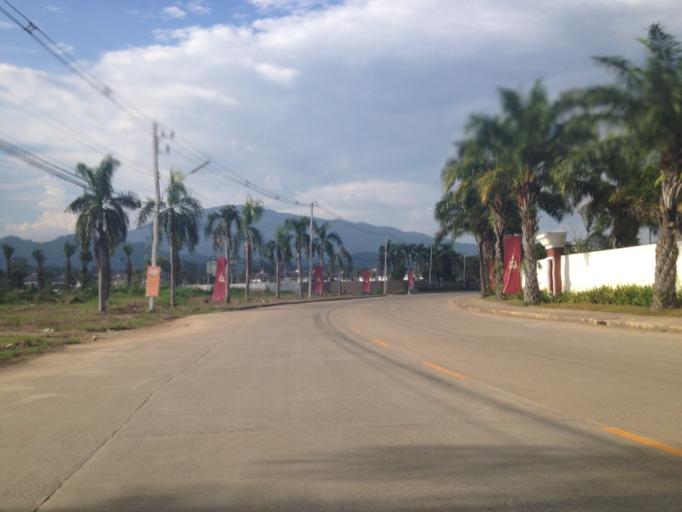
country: TH
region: Chiang Mai
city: Hang Dong
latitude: 18.7193
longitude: 98.9146
